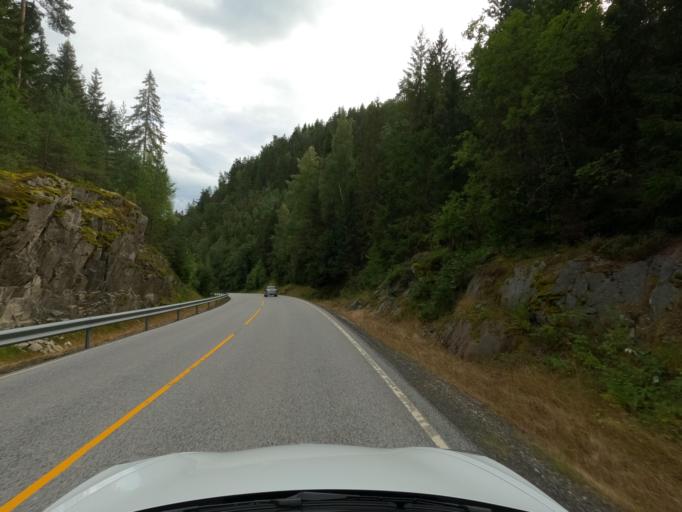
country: NO
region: Telemark
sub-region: Hjartdal
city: Sauland
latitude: 59.8204
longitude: 8.9821
